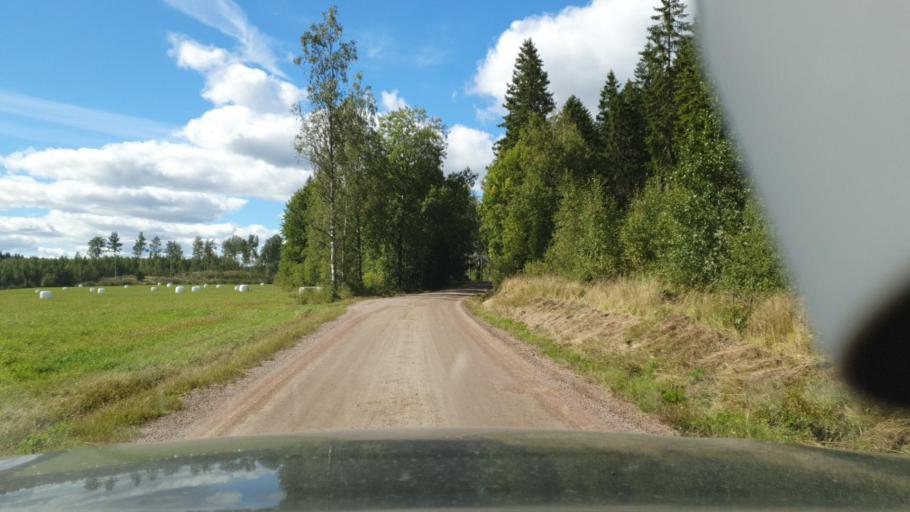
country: SE
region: Vaermland
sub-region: Storfors Kommun
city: Storfors
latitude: 59.5253
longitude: 14.1797
